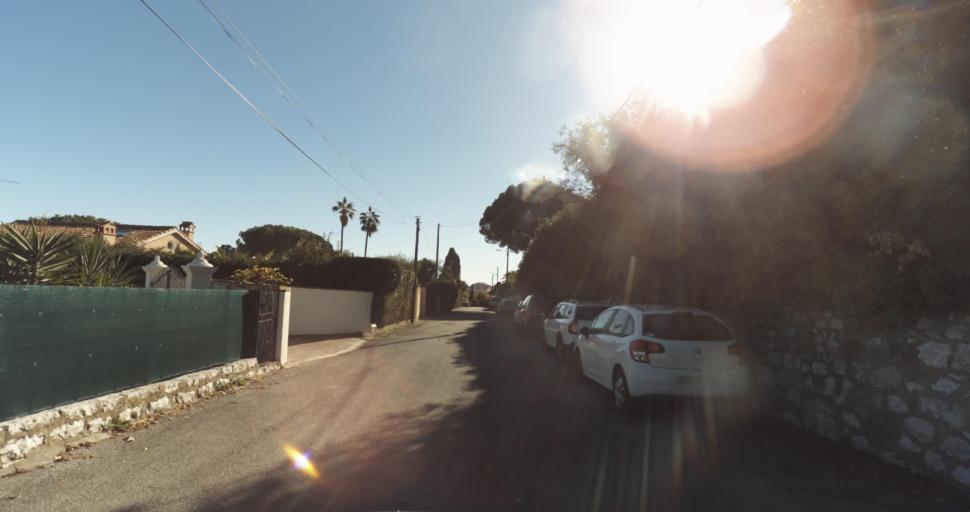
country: FR
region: Provence-Alpes-Cote d'Azur
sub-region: Departement des Alpes-Maritimes
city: Vence
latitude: 43.7191
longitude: 7.1102
